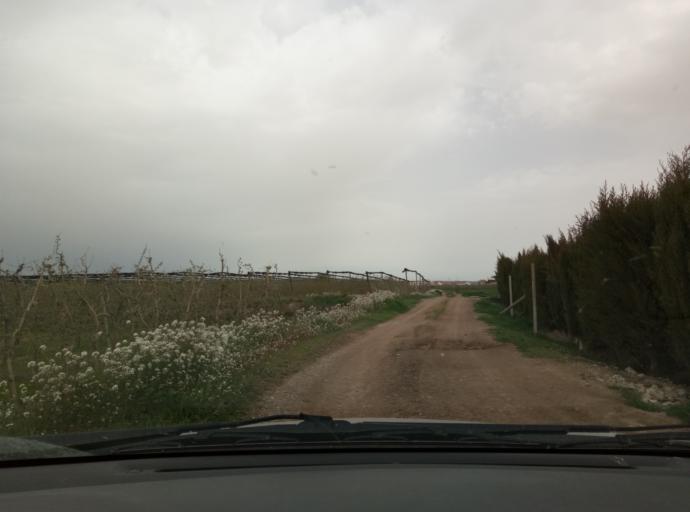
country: ES
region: Catalonia
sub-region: Provincia de Lleida
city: La Fuliola
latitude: 41.7019
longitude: 1.0267
